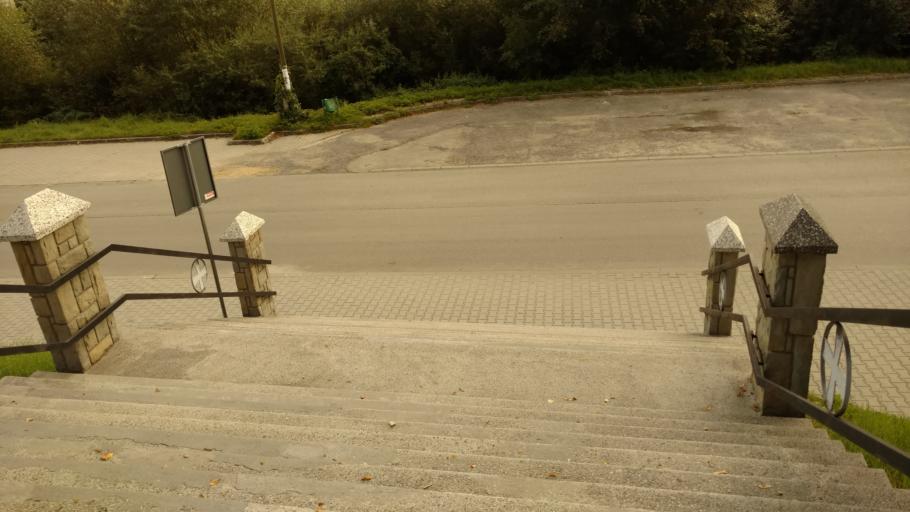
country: PL
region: Lesser Poland Voivodeship
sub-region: Powiat myslenicki
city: Skomielna Czarna
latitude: 49.7266
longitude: 19.8371
